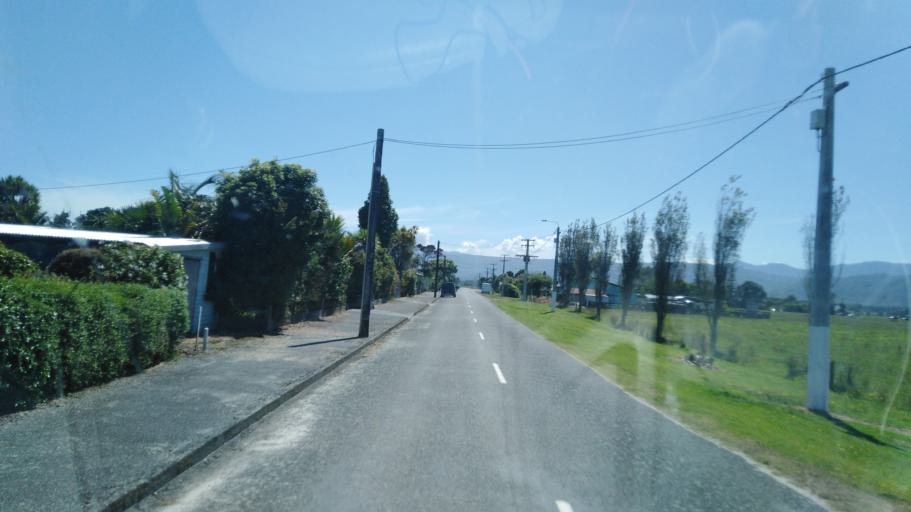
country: NZ
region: West Coast
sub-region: Buller District
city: Westport
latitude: -41.2506
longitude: 172.1104
